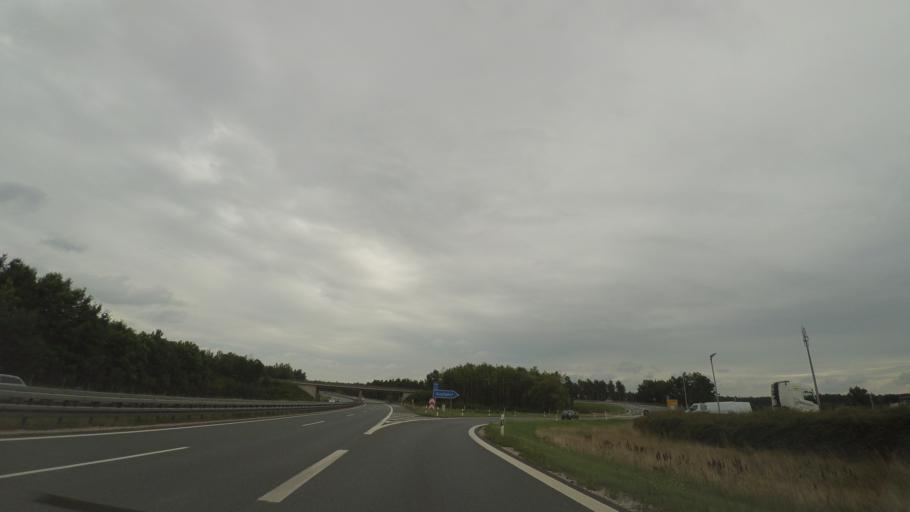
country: DE
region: Bavaria
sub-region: Upper Palatinate
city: Ebermannsdorf
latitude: 49.4000
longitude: 11.9777
